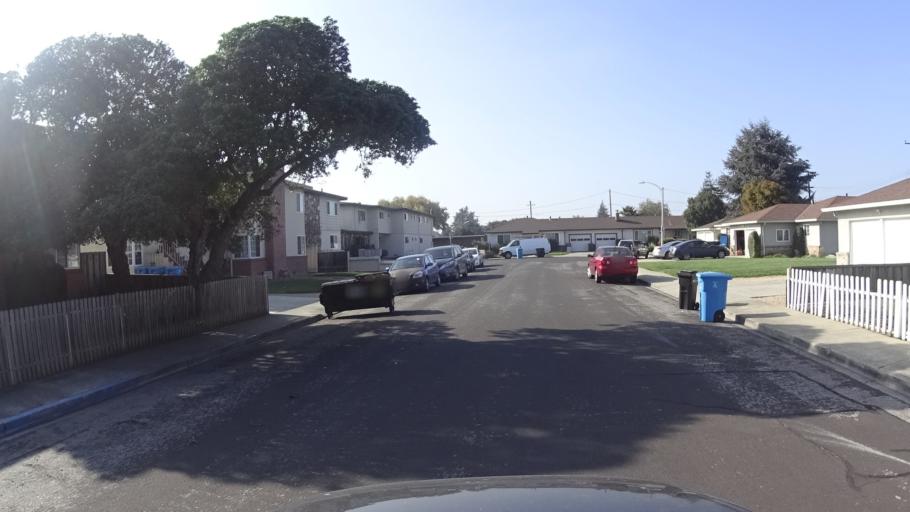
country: US
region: California
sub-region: Santa Clara County
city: Santa Clara
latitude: 37.3535
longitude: -121.9869
